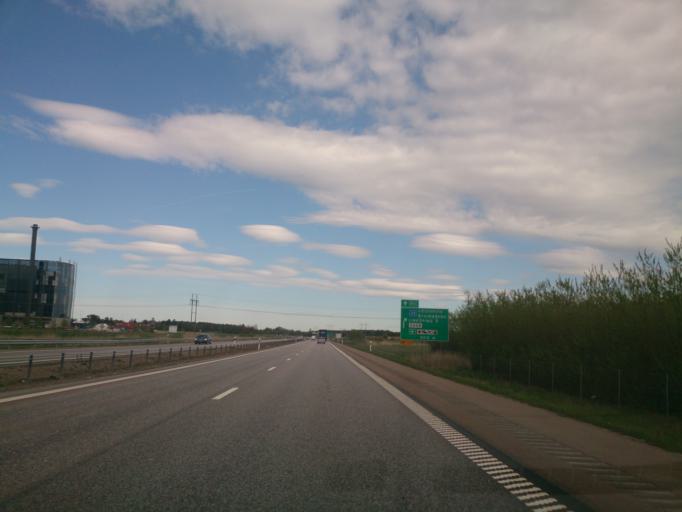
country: SE
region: OEstergoetland
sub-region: Linkopings Kommun
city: Linkoping
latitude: 58.4325
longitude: 15.6510
